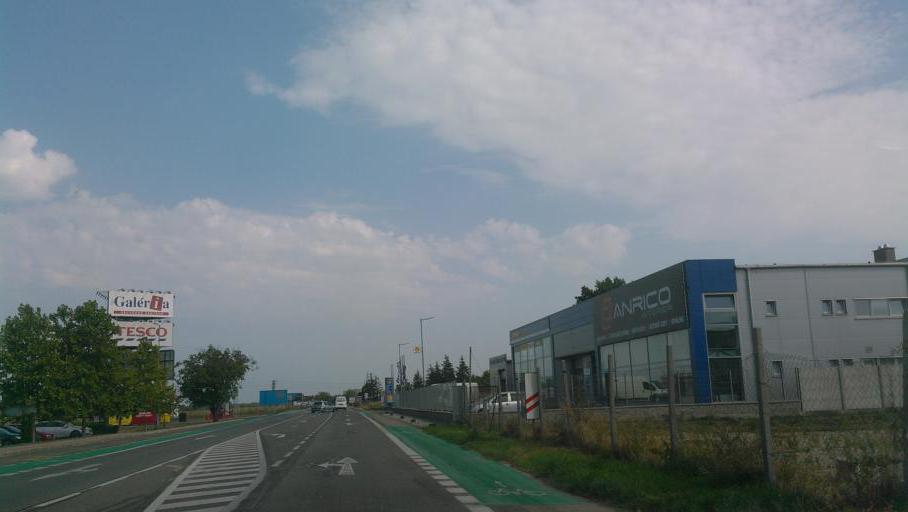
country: SK
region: Trnavsky
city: Dunajska Streda
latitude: 47.9881
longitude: 17.6318
